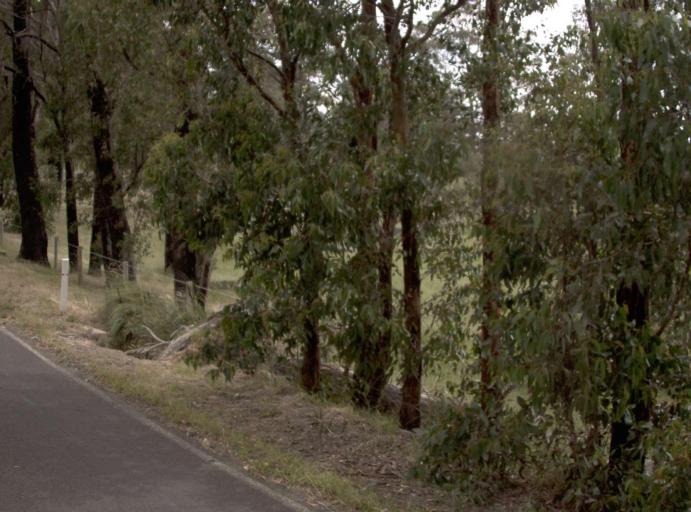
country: AU
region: Victoria
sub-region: Latrobe
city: Traralgon
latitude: -38.3177
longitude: 146.5734
